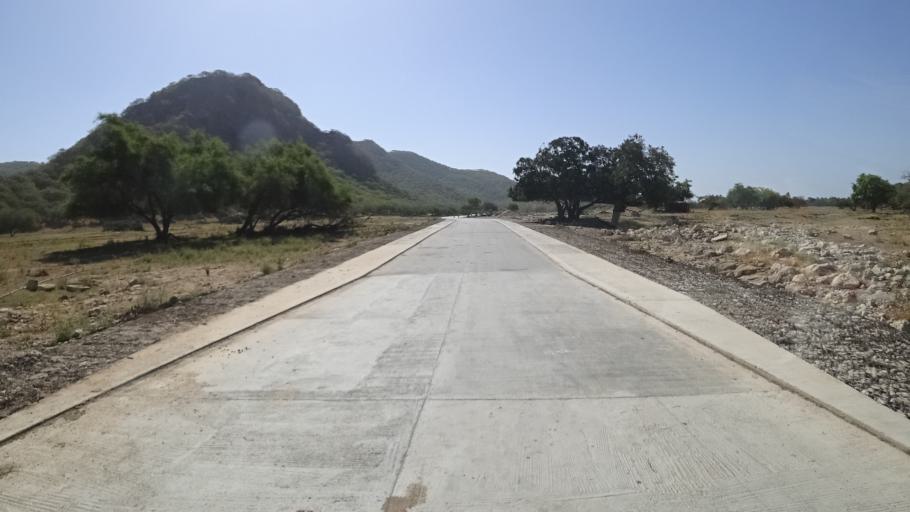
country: OM
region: Zufar
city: Salalah
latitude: 17.0882
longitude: 54.4337
